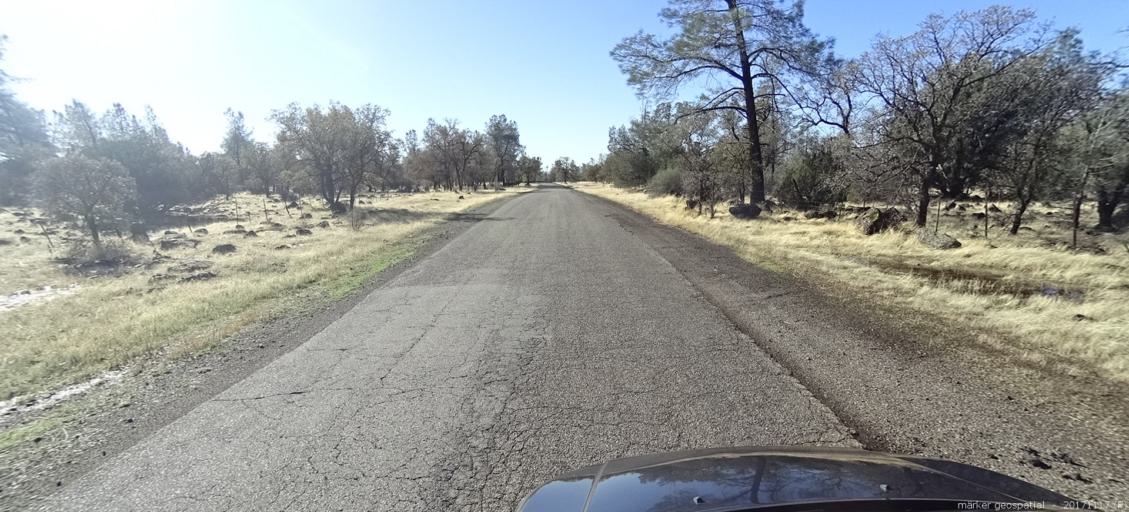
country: US
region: California
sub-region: Shasta County
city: Palo Cedro
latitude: 40.4523
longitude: -122.1103
